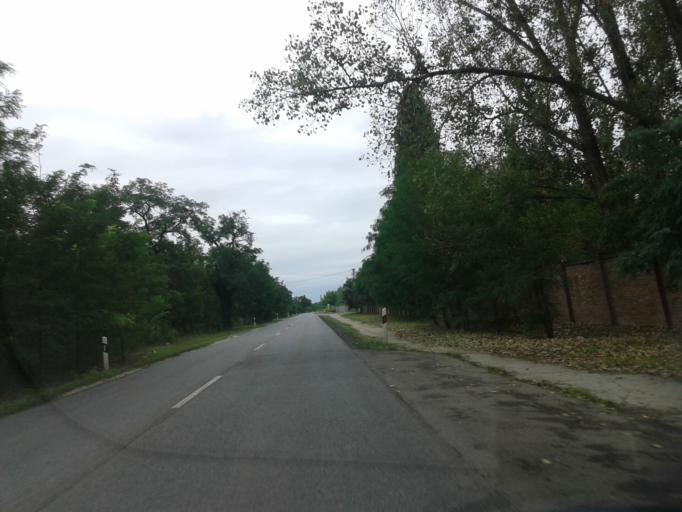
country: HU
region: Pest
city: Halasztelek
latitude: 47.3478
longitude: 18.9897
